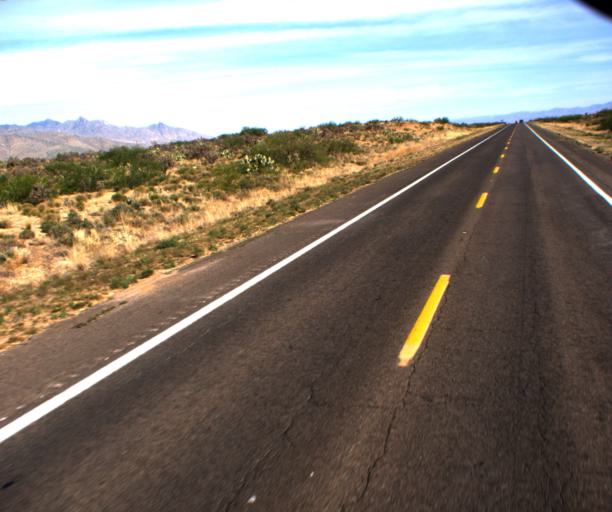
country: US
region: Arizona
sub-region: Graham County
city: Swift Trail Junction
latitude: 32.6176
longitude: -109.6885
